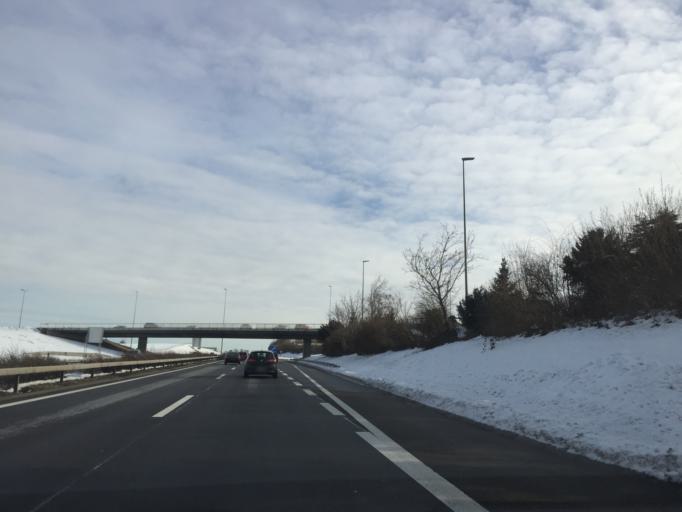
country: CH
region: Zurich
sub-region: Bezirk Horgen
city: Au / Unter-Dorf
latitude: 47.2306
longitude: 8.6316
